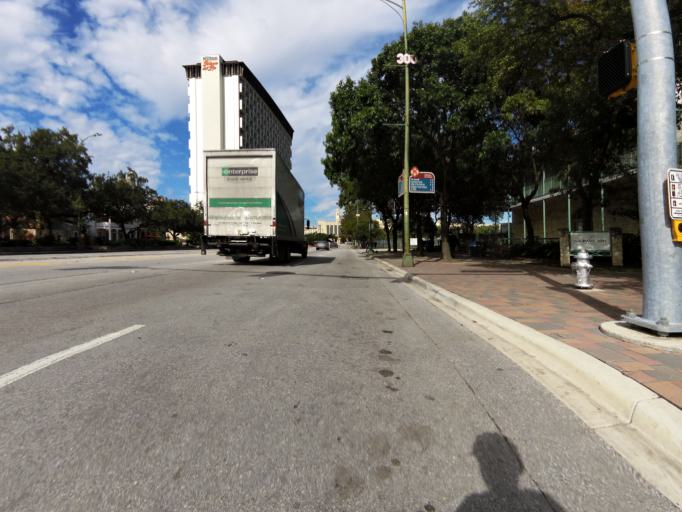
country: US
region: Texas
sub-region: Bexar County
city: San Antonio
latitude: 29.4208
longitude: -98.4879
